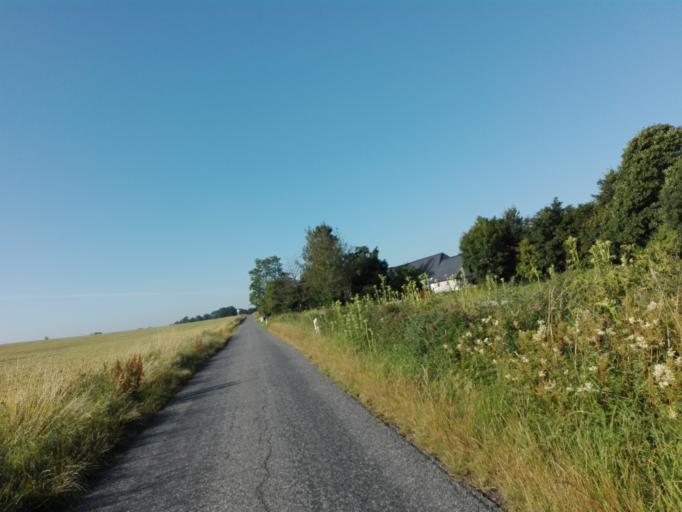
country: DK
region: Central Jutland
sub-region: Arhus Kommune
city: Tranbjerg
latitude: 56.0647
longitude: 10.1299
